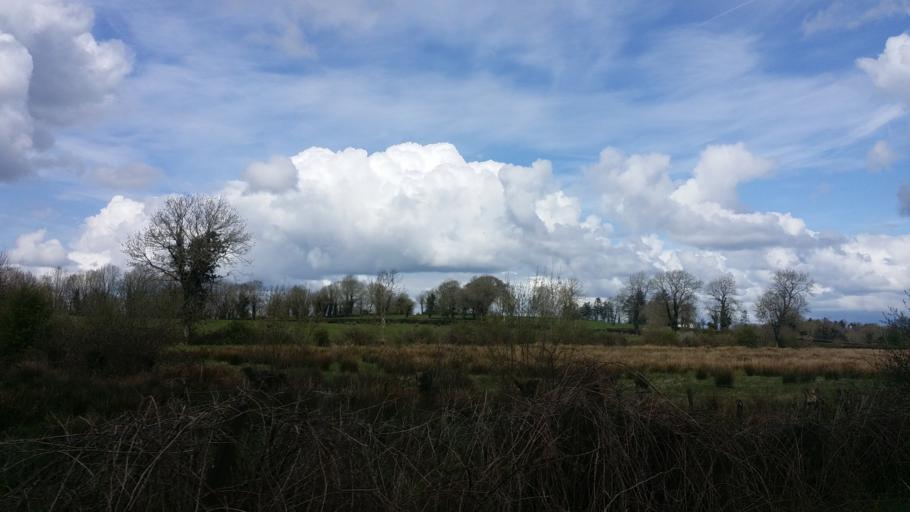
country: GB
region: Northern Ireland
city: Lisnaskea
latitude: 54.1792
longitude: -7.5014
